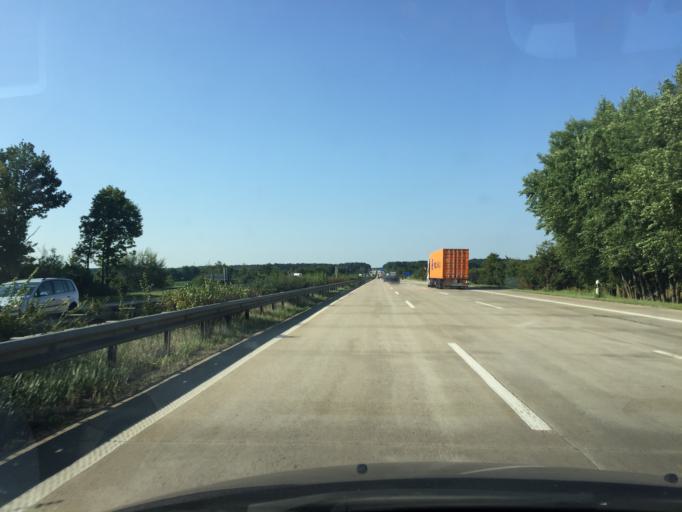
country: DE
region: Lower Saxony
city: Bispingen
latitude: 53.0991
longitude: 9.9758
